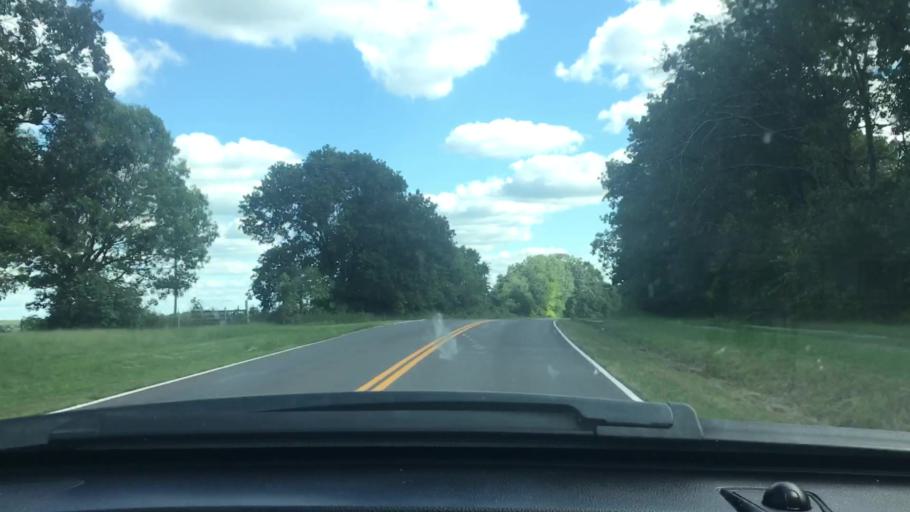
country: US
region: Missouri
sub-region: Wright County
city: Hartville
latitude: 37.3612
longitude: -92.3441
